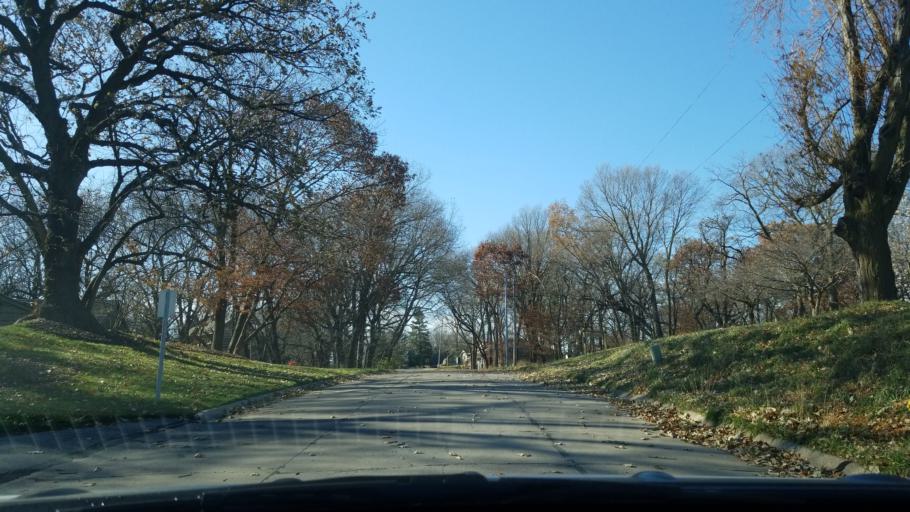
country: US
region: Nebraska
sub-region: Sarpy County
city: Bellevue
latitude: 41.1639
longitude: -95.8972
